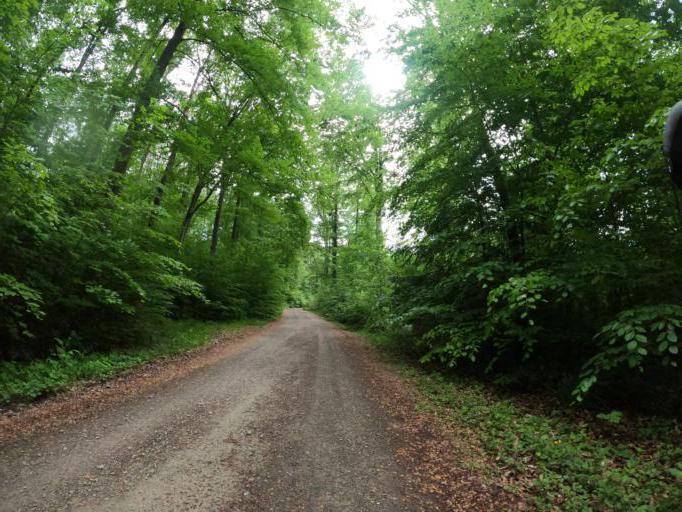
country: DE
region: Baden-Wuerttemberg
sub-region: Tuebingen Region
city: Dettenhausen
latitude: 48.5964
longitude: 9.1264
